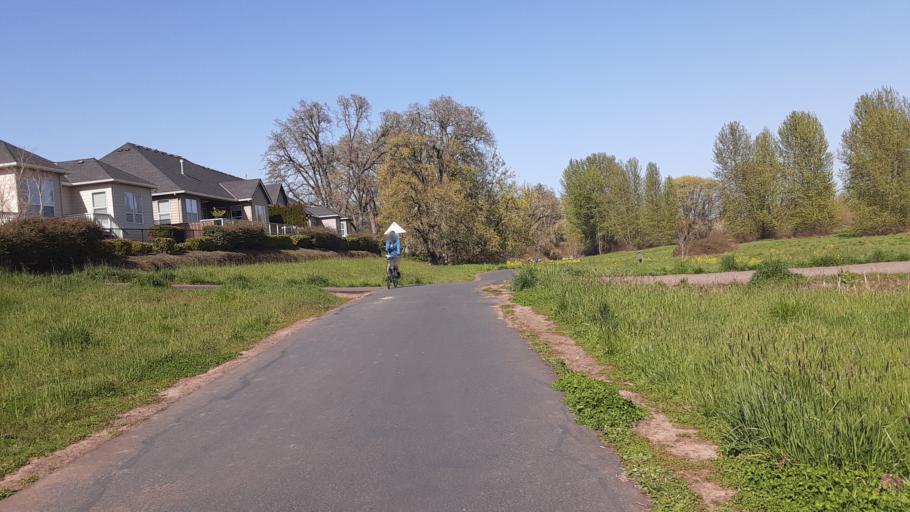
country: US
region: Oregon
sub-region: Benton County
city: Corvallis
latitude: 44.5305
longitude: -123.2540
